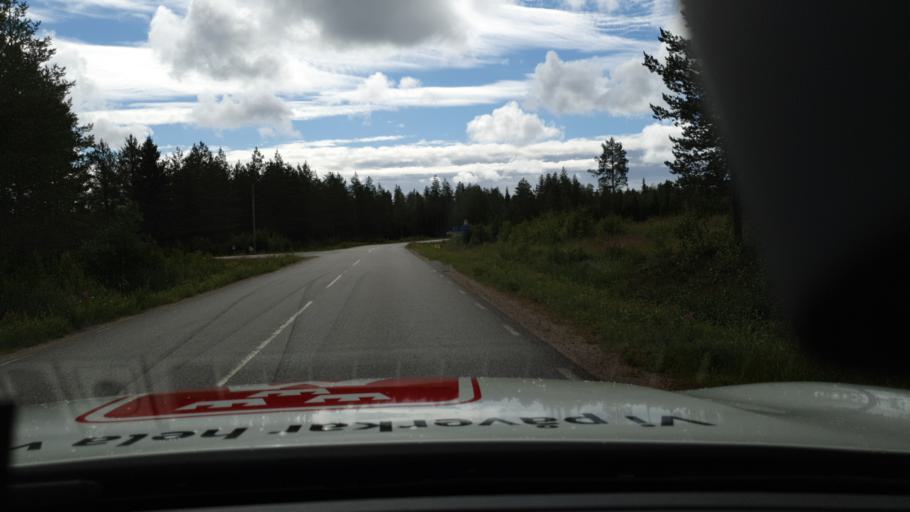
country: SE
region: Norrbotten
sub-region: Lulea Kommun
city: Sodra Sunderbyn
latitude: 65.4854
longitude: 21.9003
